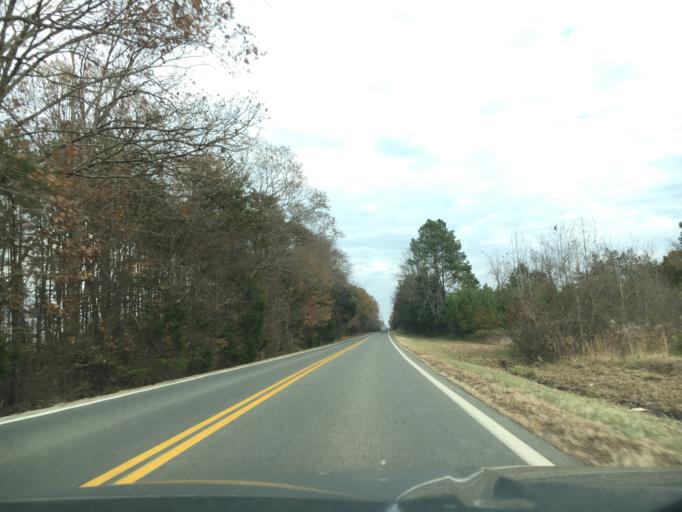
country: US
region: Virginia
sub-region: Cumberland County
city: Cumberland
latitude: 37.4414
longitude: -78.3284
